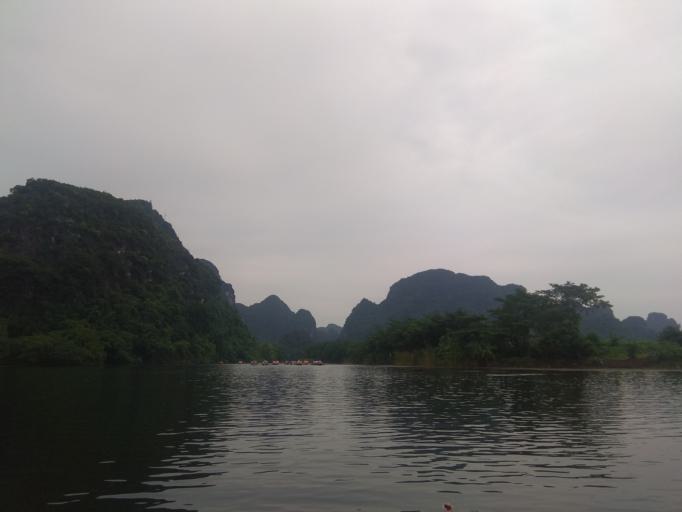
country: VN
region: Ninh Binh
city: Thi Tran Thien Ton
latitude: 20.2549
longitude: 105.9153
